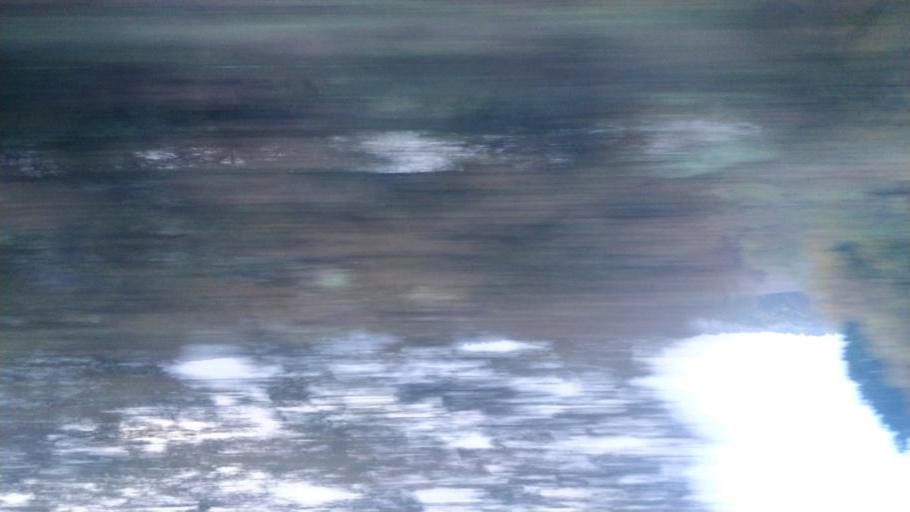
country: GB
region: England
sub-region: Lancashire
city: Appley Bridge
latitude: 53.5817
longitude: -2.7308
